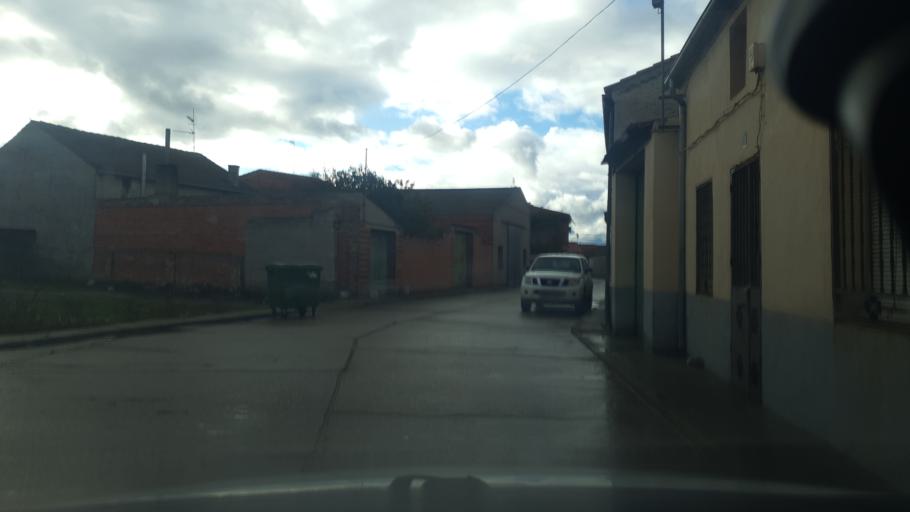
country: ES
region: Castille and Leon
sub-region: Provincia de Segovia
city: Sanchonuno
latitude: 41.2894
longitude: -4.3258
